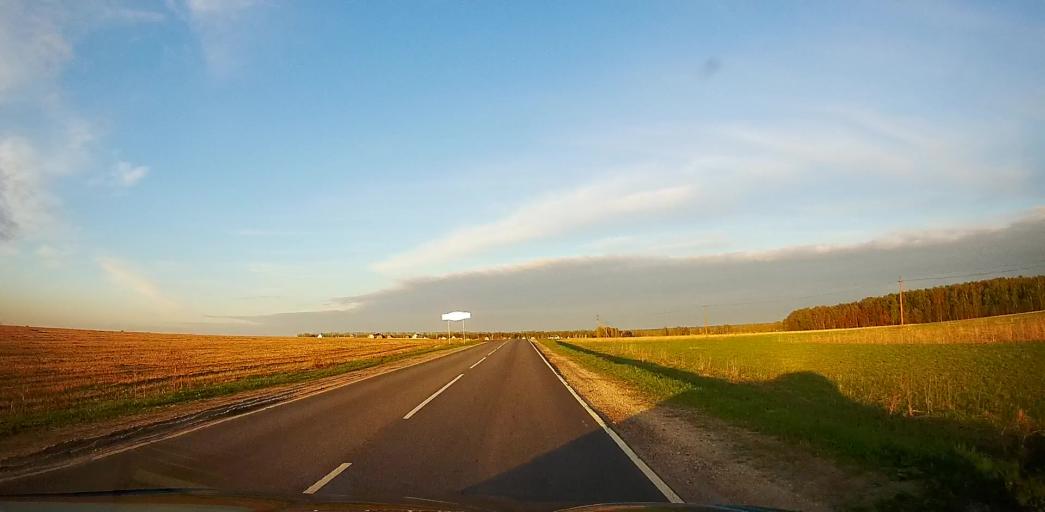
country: RU
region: Moskovskaya
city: Peski
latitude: 55.2106
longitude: 38.6830
